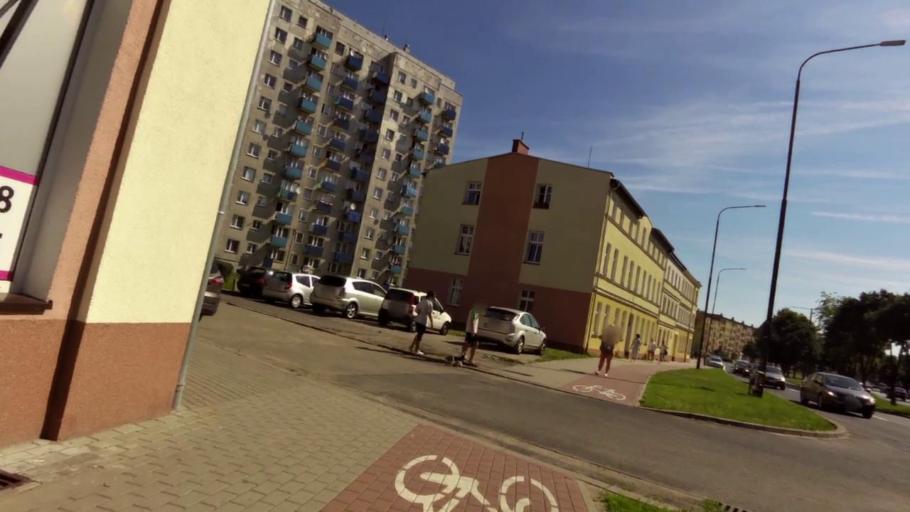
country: PL
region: West Pomeranian Voivodeship
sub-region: Powiat kolobrzeski
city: Kolobrzeg
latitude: 54.1757
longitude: 15.5856
